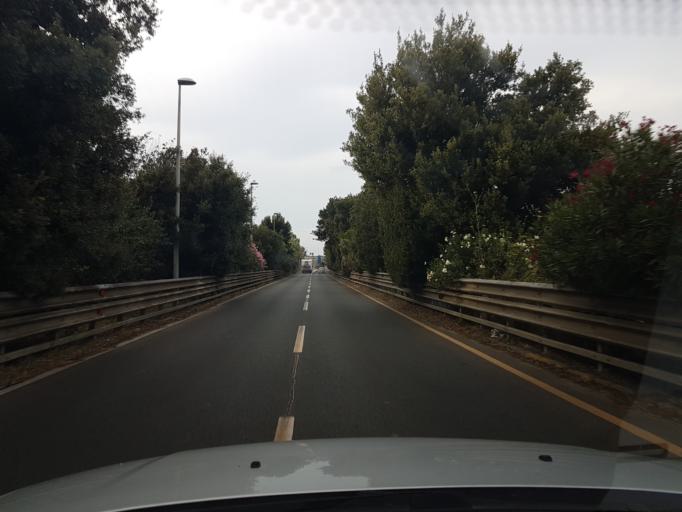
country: IT
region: Sardinia
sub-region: Provincia di Oristano
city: Donigala Fenugheddu
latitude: 39.9235
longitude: 8.5809
